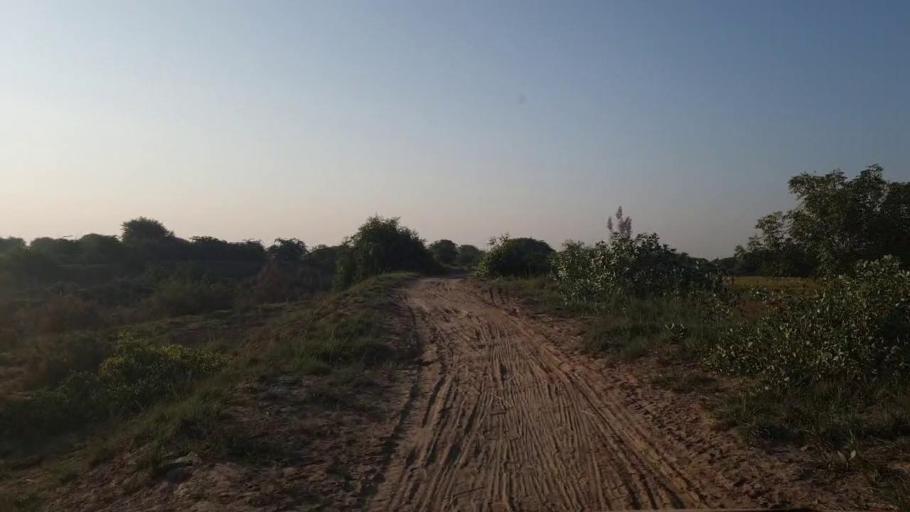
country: PK
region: Sindh
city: Badin
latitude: 24.6289
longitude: 68.7962
